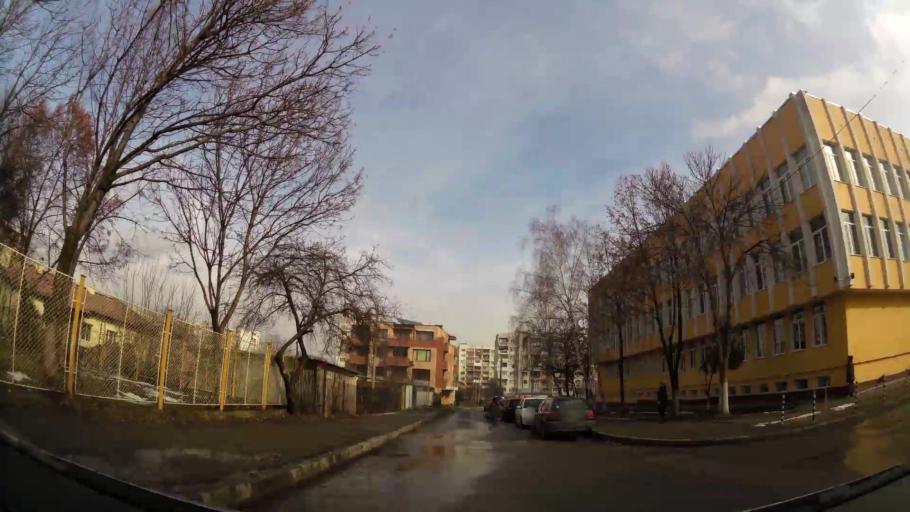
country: BG
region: Sofia-Capital
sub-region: Stolichna Obshtina
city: Sofia
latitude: 42.7183
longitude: 23.2676
